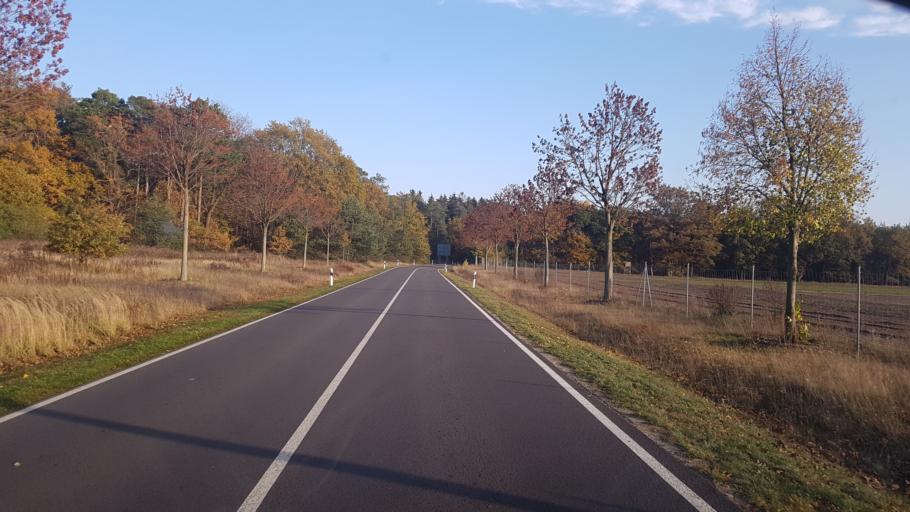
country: DE
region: Brandenburg
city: Bronkow
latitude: 51.6615
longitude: 13.9134
